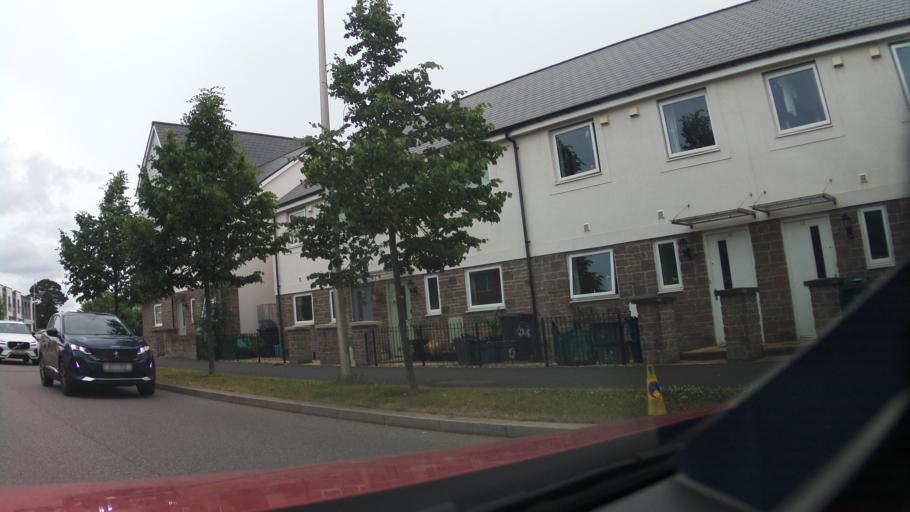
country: GB
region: England
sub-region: Devon
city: Topsham
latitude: 50.7464
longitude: -3.4164
